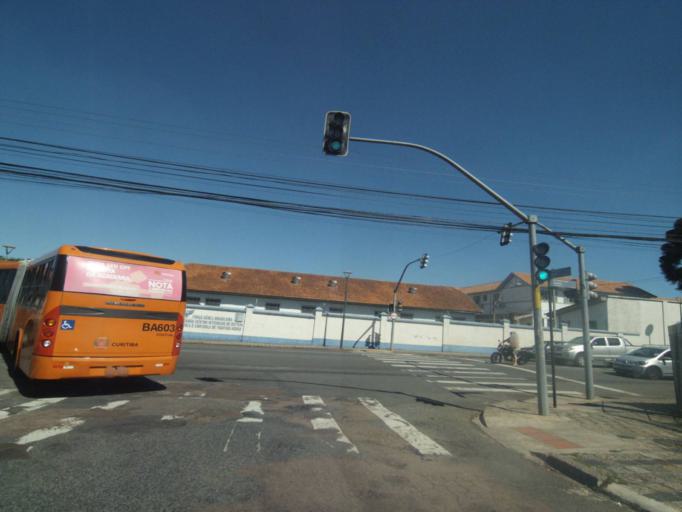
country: BR
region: Parana
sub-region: Curitiba
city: Curitiba
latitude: -25.3989
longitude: -49.2366
